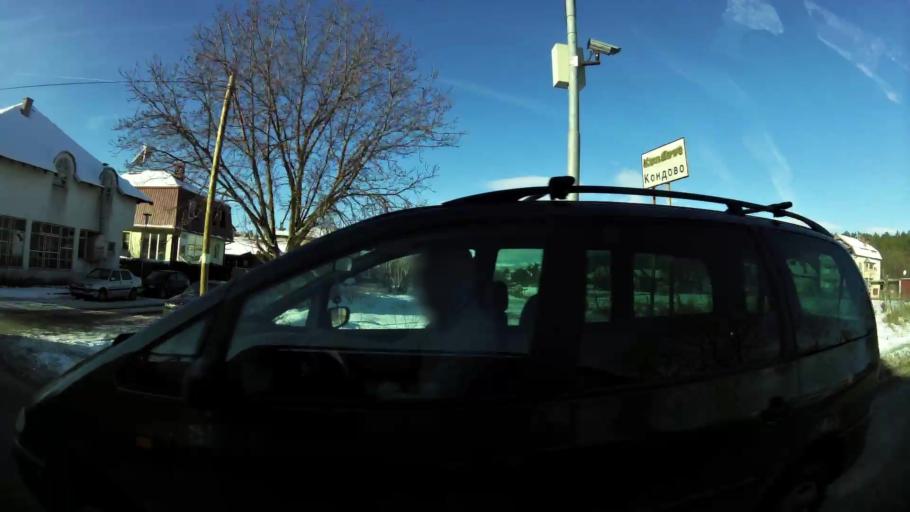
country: MK
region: Saraj
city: Saraj
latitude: 42.0095
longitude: 21.3332
